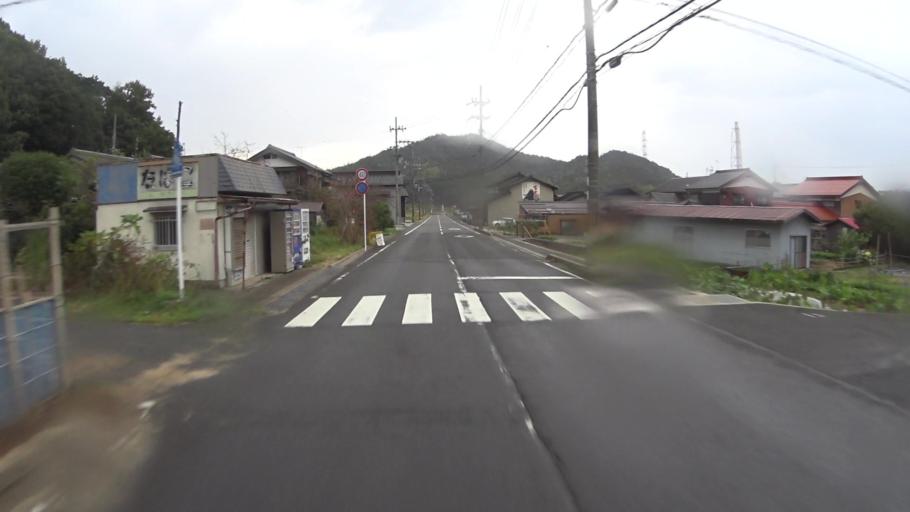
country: JP
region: Kyoto
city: Miyazu
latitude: 35.5625
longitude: 135.2446
